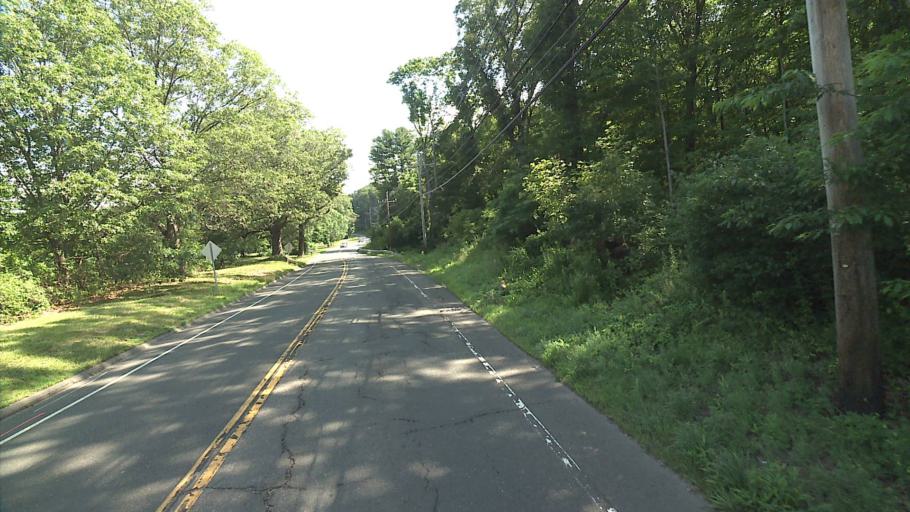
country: US
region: Connecticut
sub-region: Middlesex County
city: Westbrook Center
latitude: 41.3012
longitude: -72.4391
